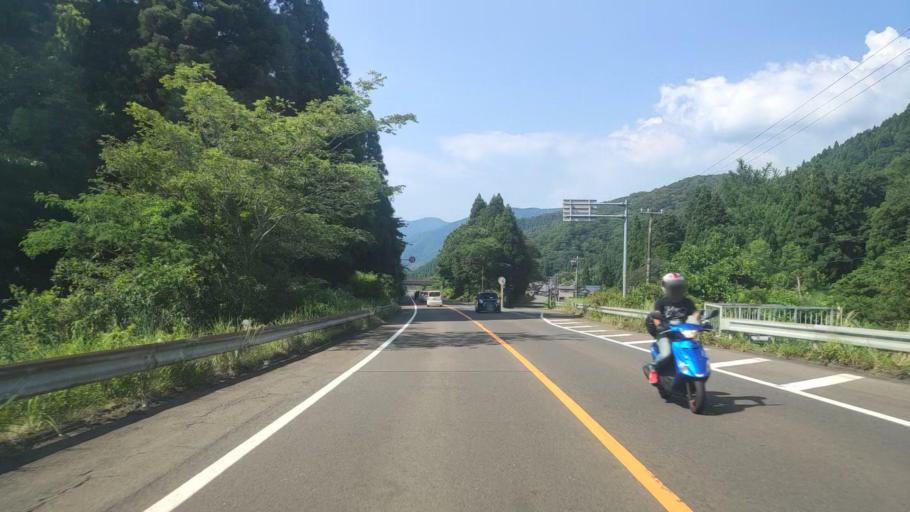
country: JP
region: Fukui
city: Tsuruga
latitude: 35.5834
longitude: 136.1246
